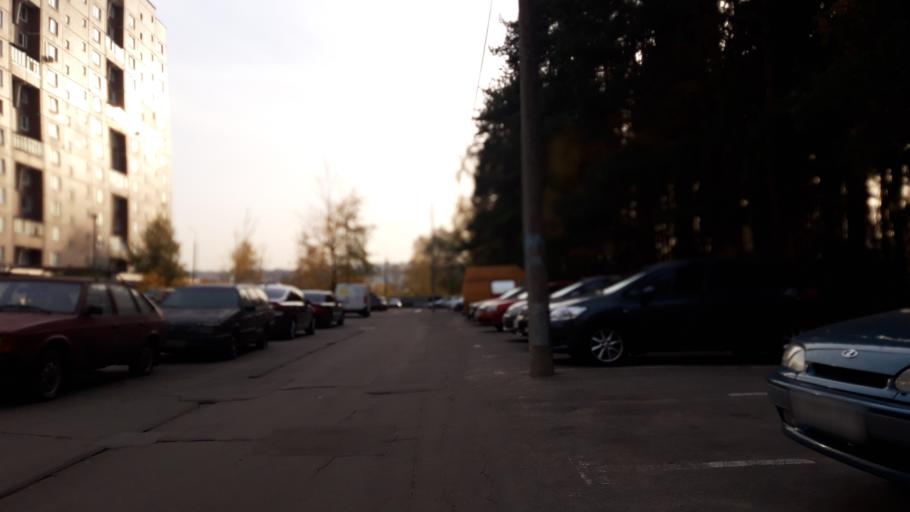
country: RU
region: Moscow
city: Zelenograd
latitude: 55.9945
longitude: 37.1694
